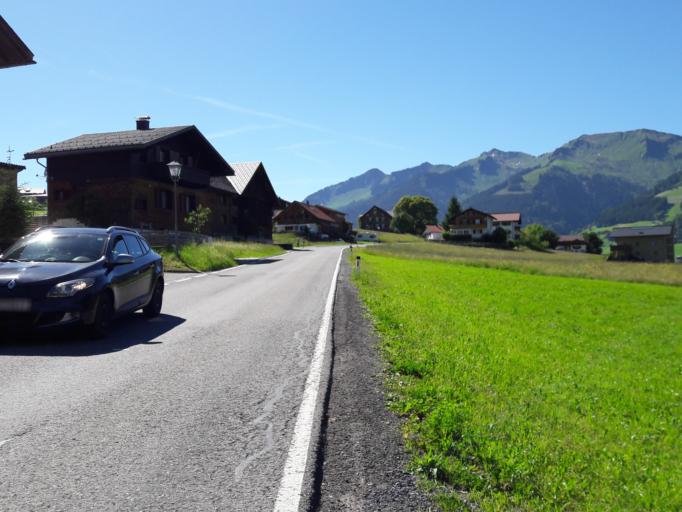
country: AT
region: Vorarlberg
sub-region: Politischer Bezirk Bludenz
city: Raggal
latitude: 47.2109
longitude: 9.8431
